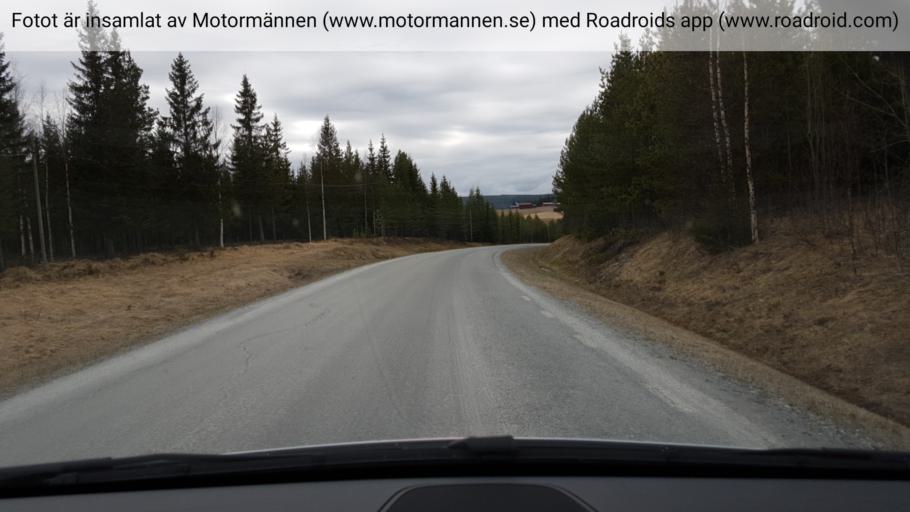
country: SE
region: Jaemtland
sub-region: Bergs Kommun
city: Hoverberg
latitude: 62.9719
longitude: 14.2857
